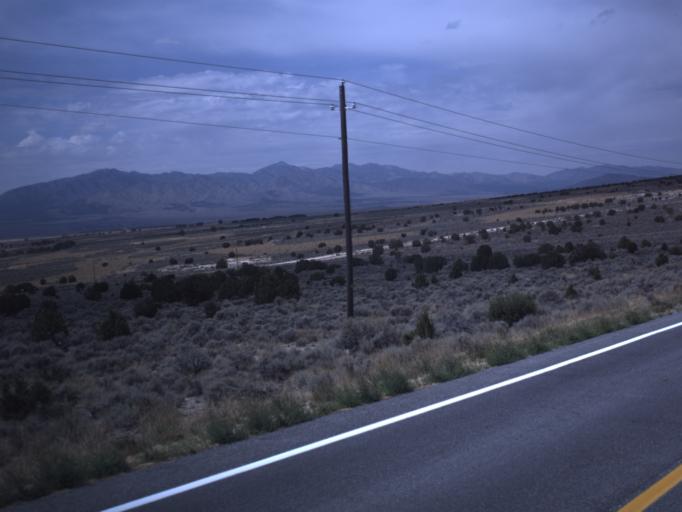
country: US
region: Utah
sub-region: Tooele County
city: Tooele
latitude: 40.3181
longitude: -112.2851
